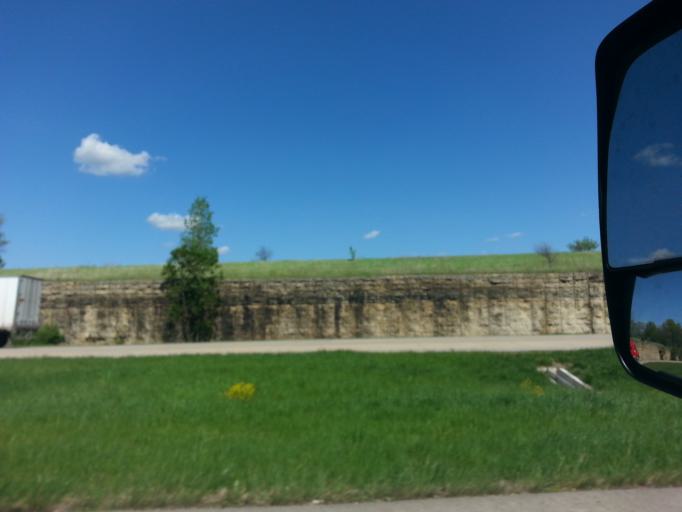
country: US
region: Illinois
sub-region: Winnebago County
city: Cherry Valley
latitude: 42.1785
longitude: -89.0239
